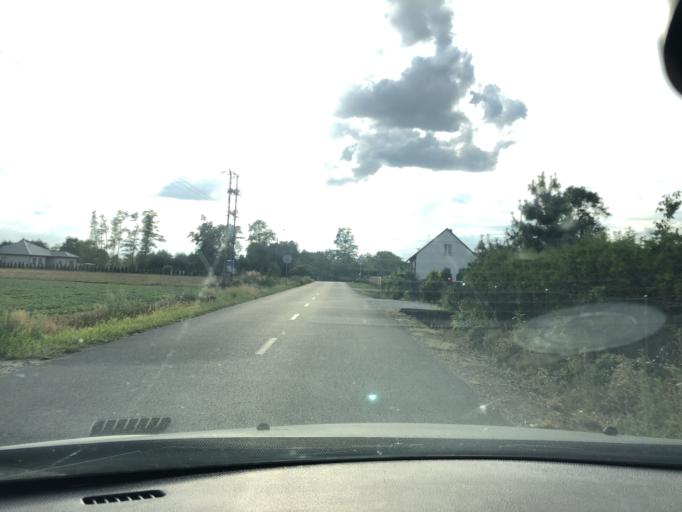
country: PL
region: Lodz Voivodeship
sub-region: Powiat wieruszowski
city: Walichnowy
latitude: 51.2456
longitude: 18.3734
